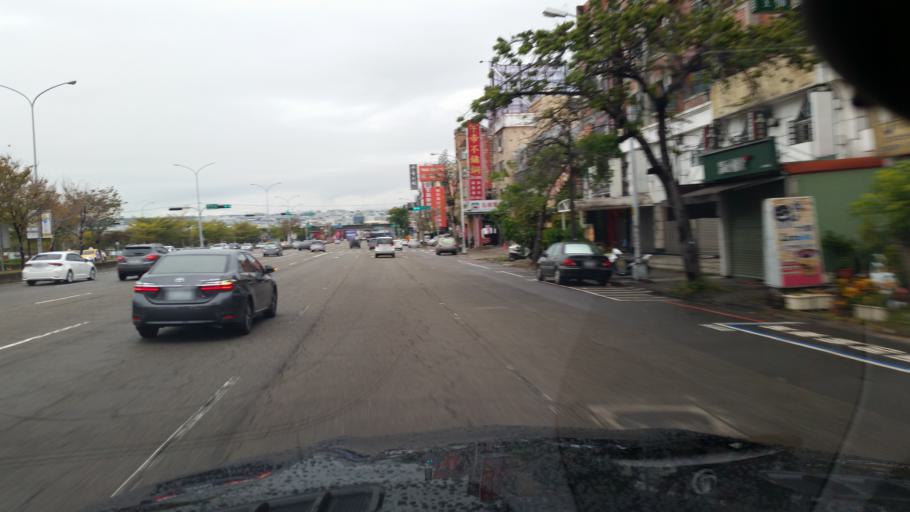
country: TW
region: Taiwan
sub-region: Taichung City
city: Taichung
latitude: 24.1618
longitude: 120.6331
